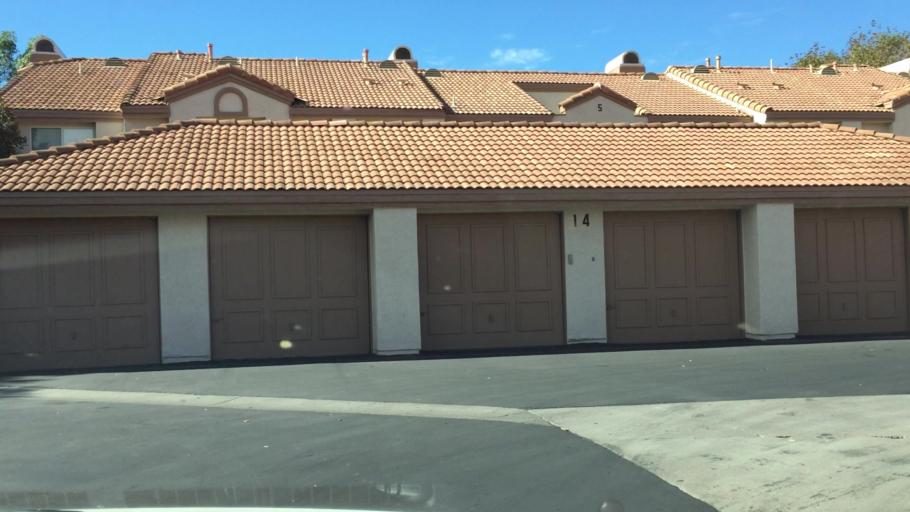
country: US
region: California
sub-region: Orange County
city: Lake Forest
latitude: 33.6585
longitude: -117.6728
